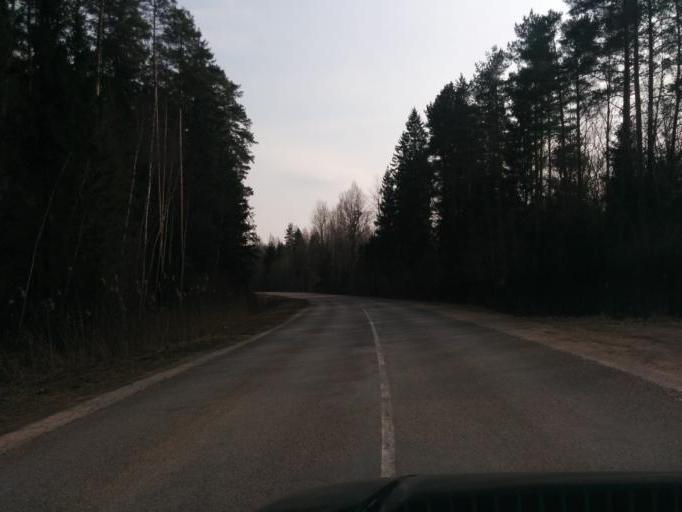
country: LV
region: Kekava
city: Balozi
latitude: 56.7875
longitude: 24.0767
